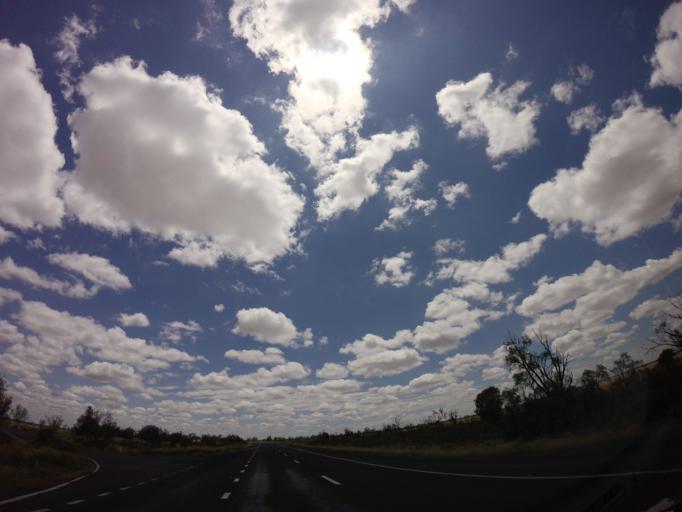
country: AU
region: New South Wales
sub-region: Moree Plains
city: Moree
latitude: -29.0403
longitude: 150.0521
